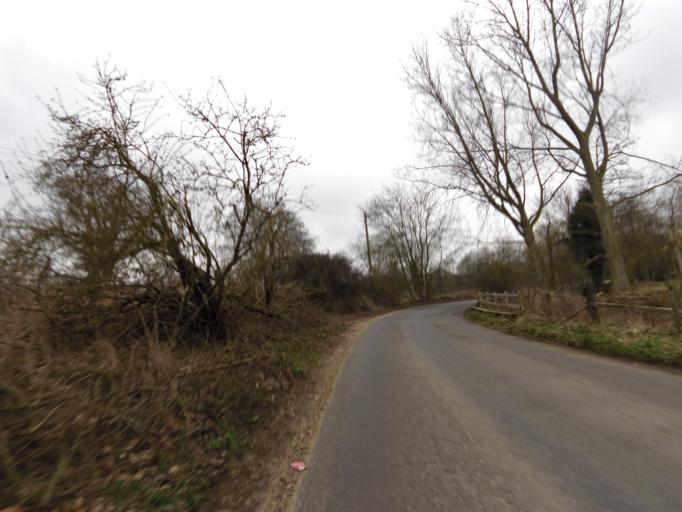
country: GB
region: England
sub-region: Suffolk
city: Wickham Market
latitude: 52.1608
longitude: 1.3566
